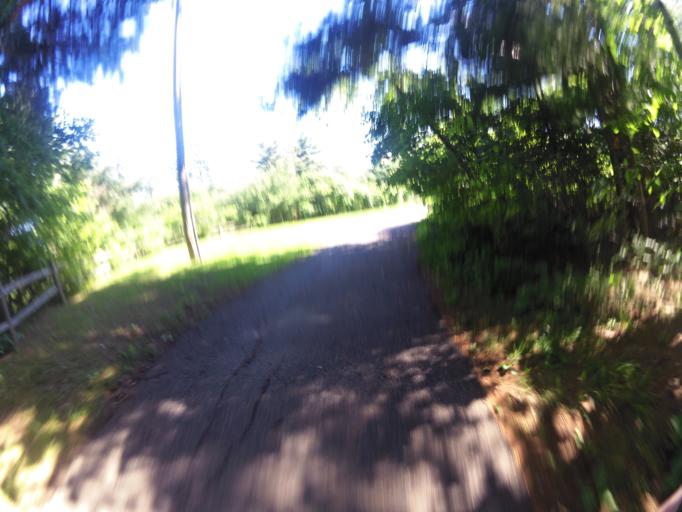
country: CA
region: Ontario
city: Bells Corners
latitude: 45.3264
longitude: -75.7860
